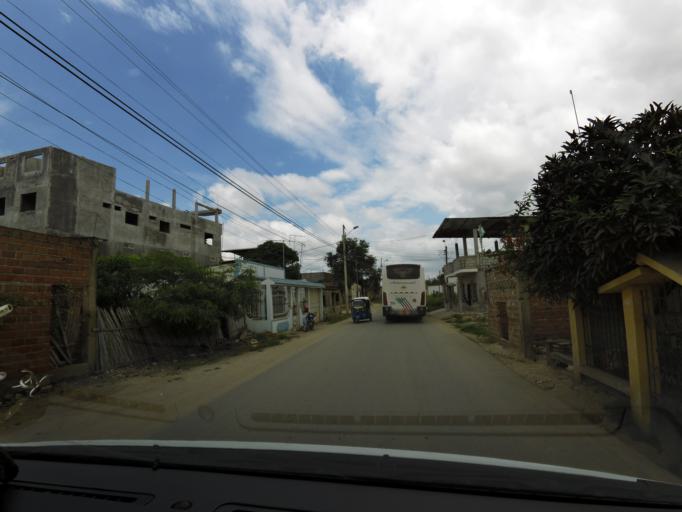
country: EC
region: El Oro
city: Huaquillas
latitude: -3.4840
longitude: -80.2258
